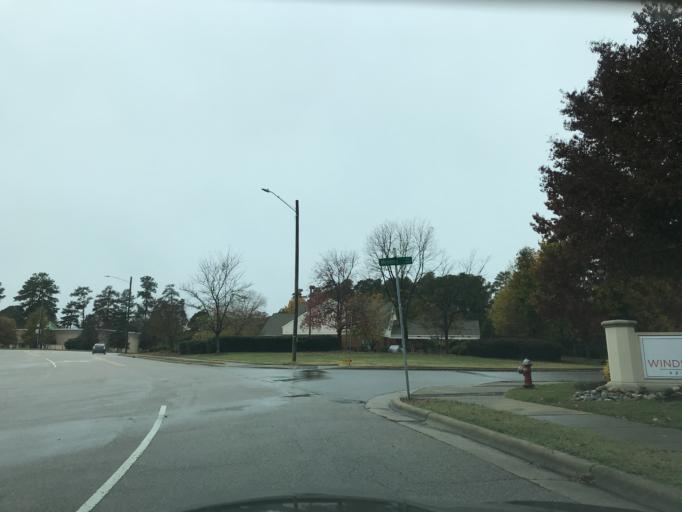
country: US
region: North Carolina
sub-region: Wake County
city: Raleigh
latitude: 35.8446
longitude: -78.6114
